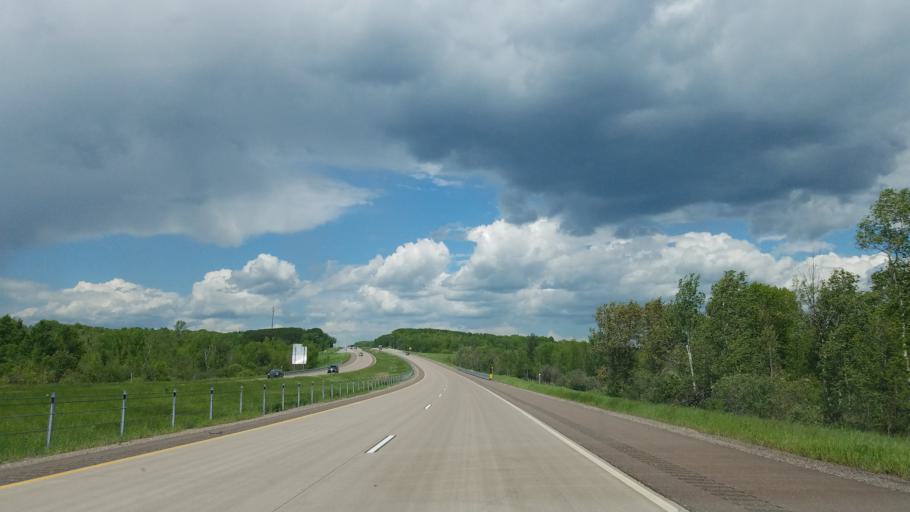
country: US
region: Minnesota
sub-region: Carlton County
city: Moose Lake
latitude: 46.4478
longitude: -92.7352
